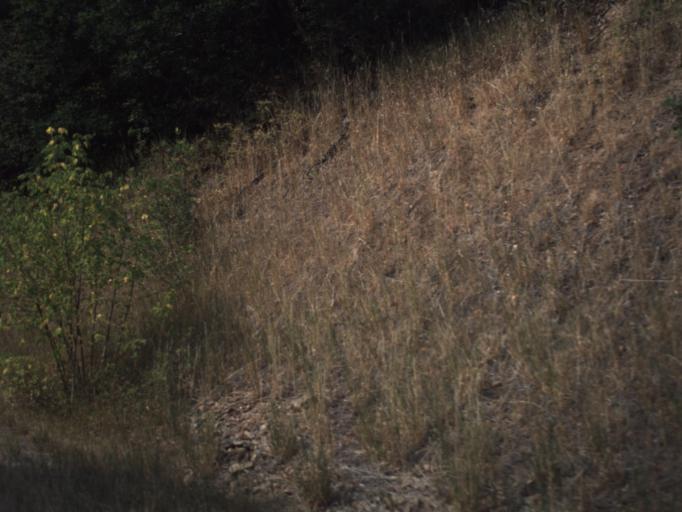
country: US
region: Utah
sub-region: Summit County
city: Summit Park
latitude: 40.7978
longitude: -111.6803
